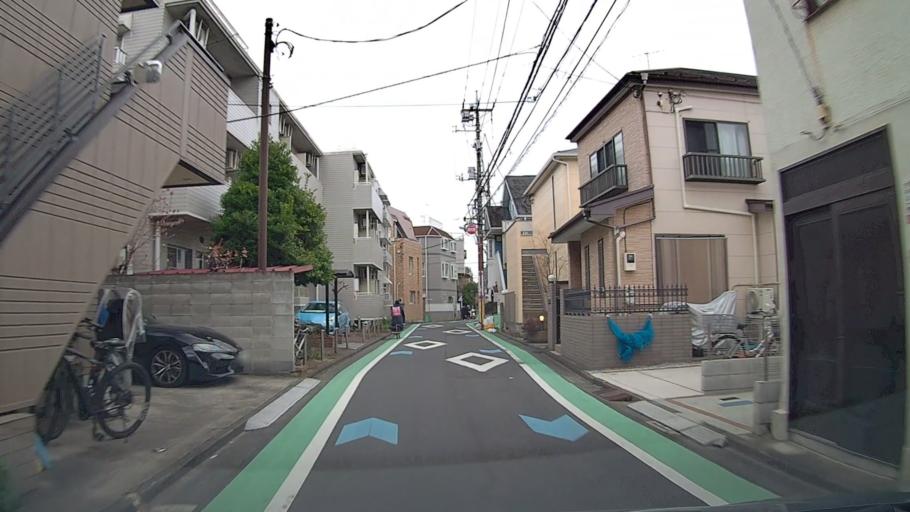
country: JP
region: Tokyo
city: Tokyo
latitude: 35.7093
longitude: 139.6458
